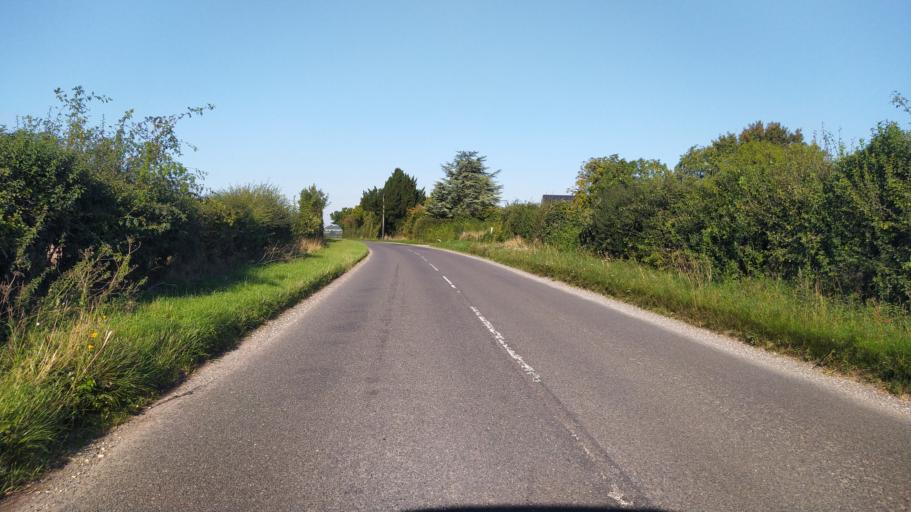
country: GB
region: England
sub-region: Hampshire
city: Abbotts Ann
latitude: 51.1619
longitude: -1.5771
